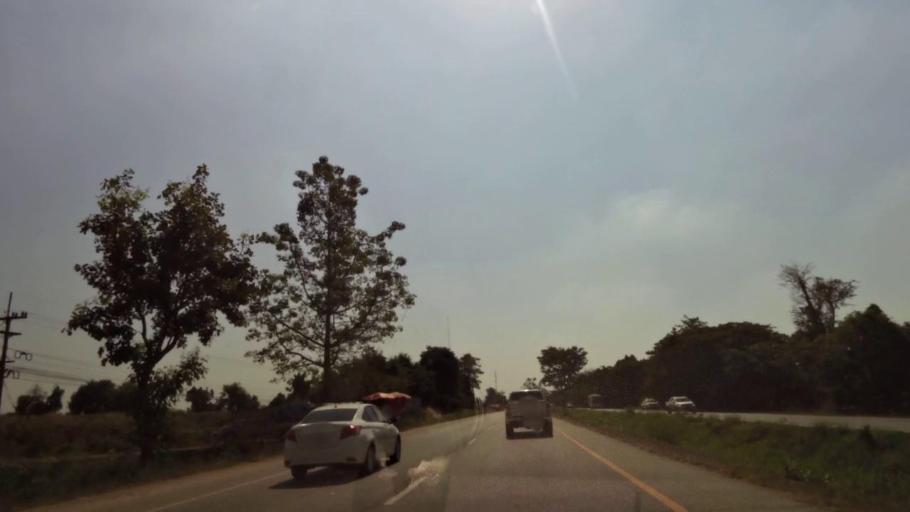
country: TH
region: Phichit
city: Wachira Barami
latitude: 16.4200
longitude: 100.1440
